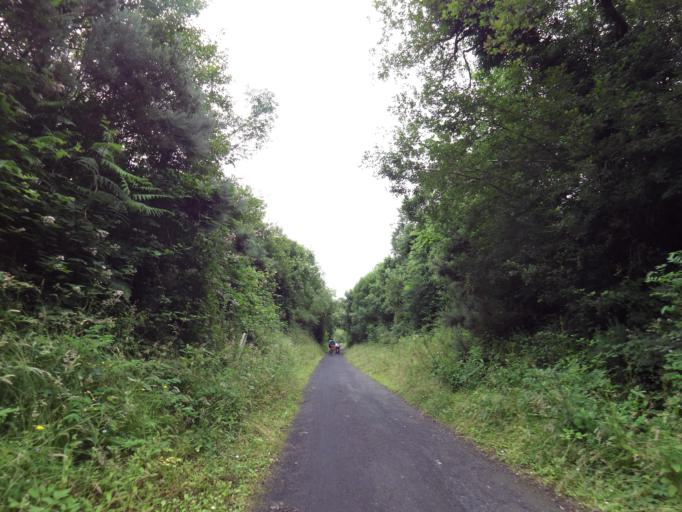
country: IE
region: Connaught
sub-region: Maigh Eo
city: Westport
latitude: 53.8181
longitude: -9.5351
